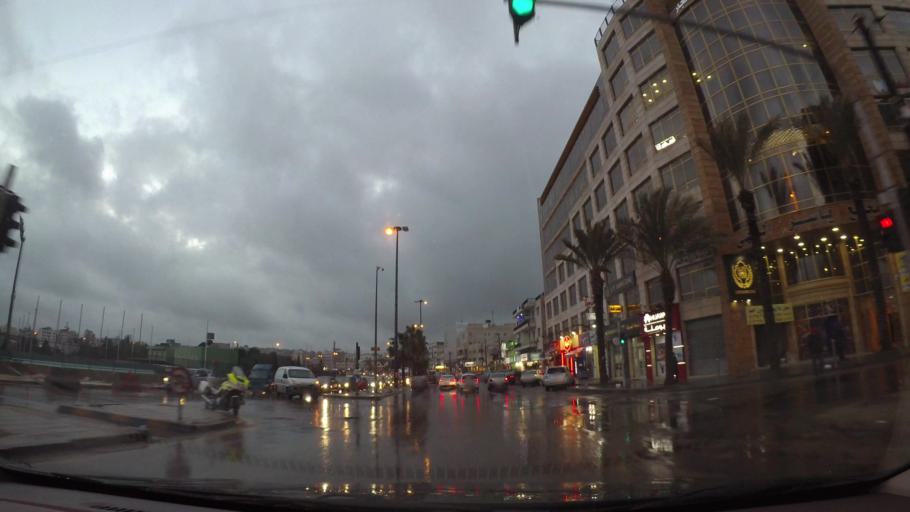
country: JO
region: Amman
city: Amman
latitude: 31.9874
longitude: 35.9032
